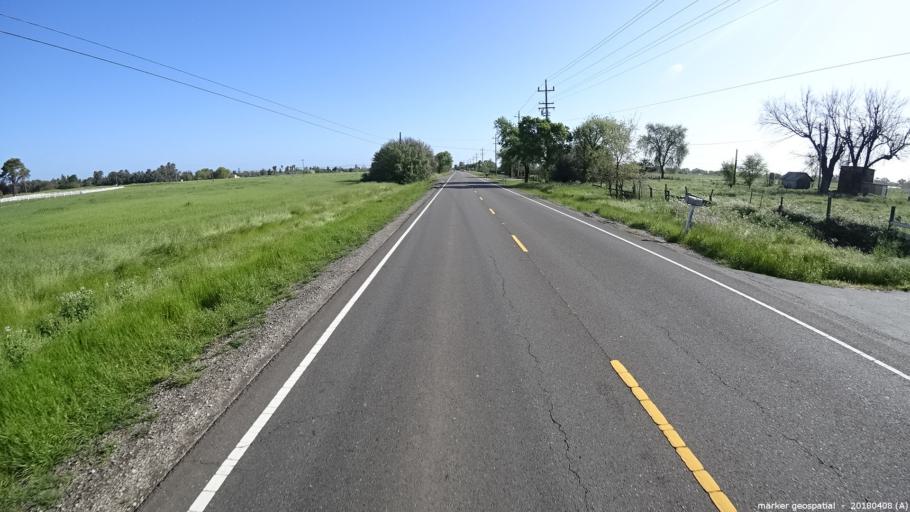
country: US
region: California
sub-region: Sacramento County
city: Elk Grove
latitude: 38.4069
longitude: -121.3268
